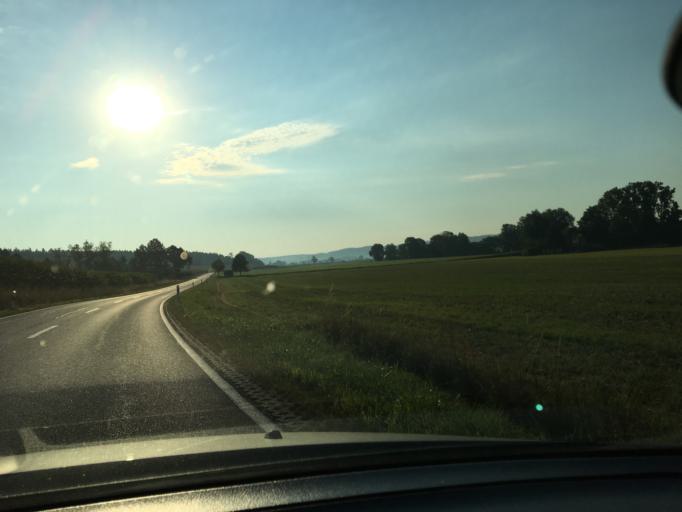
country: DE
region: Bavaria
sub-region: Lower Bavaria
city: Schalkham
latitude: 48.4985
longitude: 12.3866
